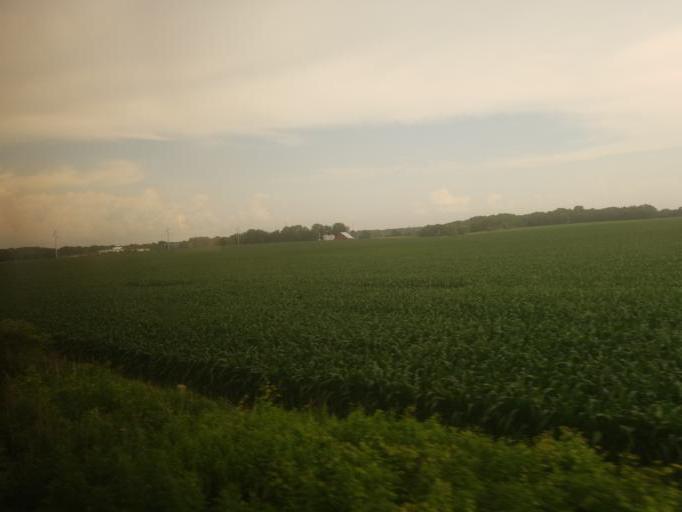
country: US
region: Illinois
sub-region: Bureau County
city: Princeton
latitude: 41.3932
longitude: -89.4986
